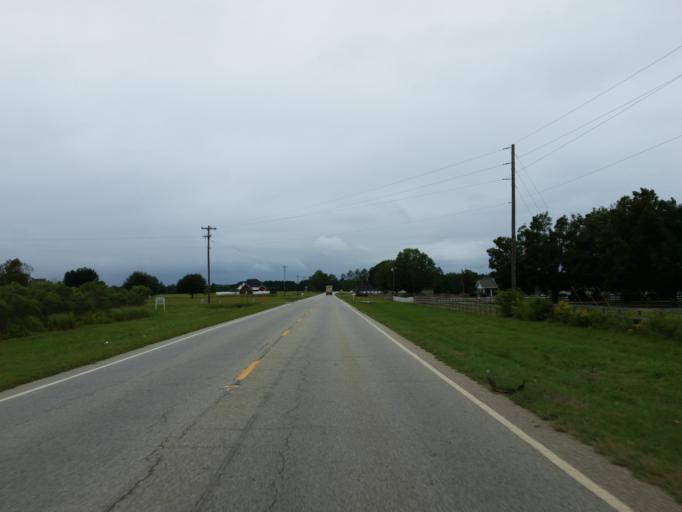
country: US
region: Georgia
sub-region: Cook County
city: Adel
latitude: 31.1310
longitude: -83.3546
